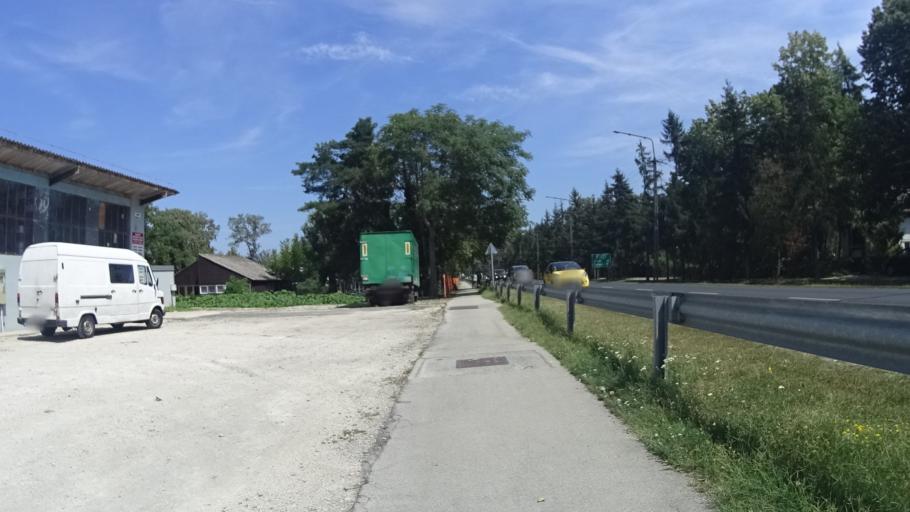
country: HU
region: Somogy
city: Balatonfenyves
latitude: 46.7304
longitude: 17.5300
